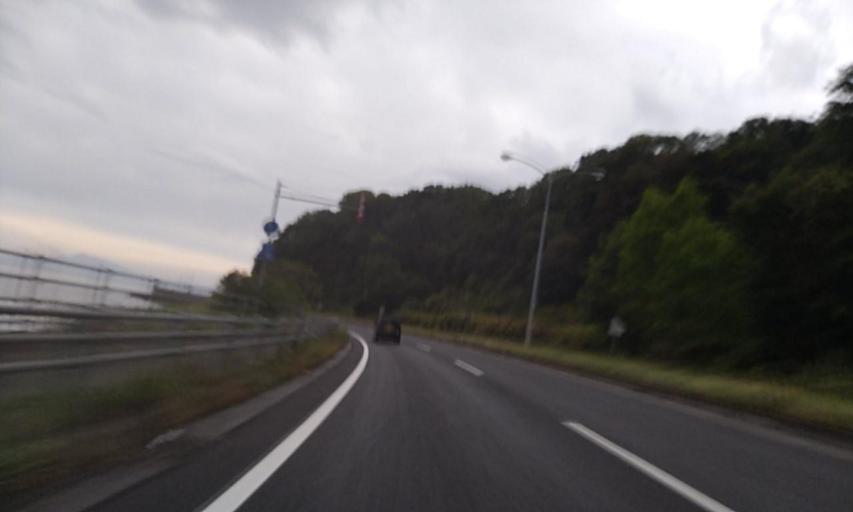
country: JP
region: Hokkaido
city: Abashiri
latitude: 44.0038
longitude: 144.2867
